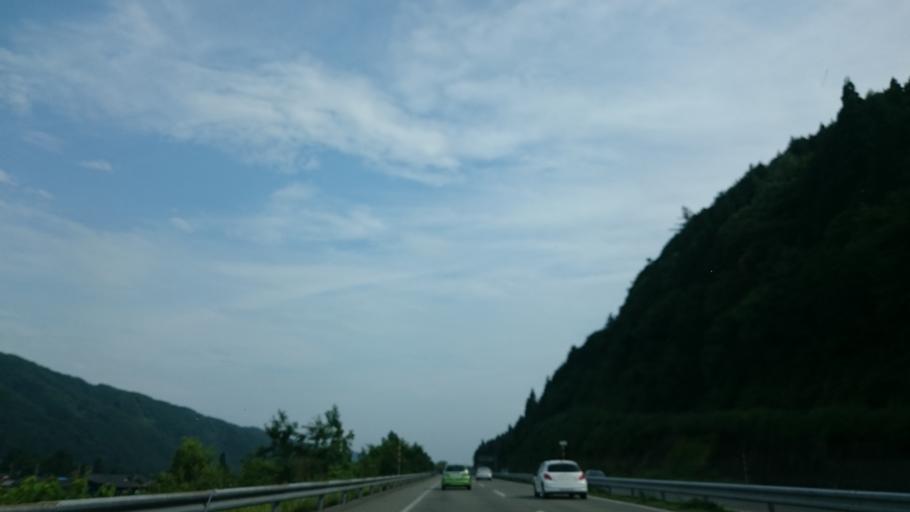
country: JP
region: Gifu
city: Gujo
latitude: 35.8445
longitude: 136.8735
